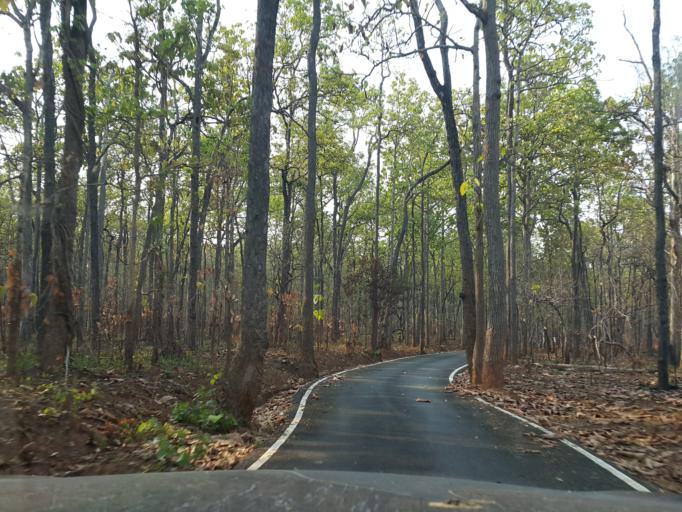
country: TH
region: Lamphun
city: Li
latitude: 17.6389
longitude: 98.8809
